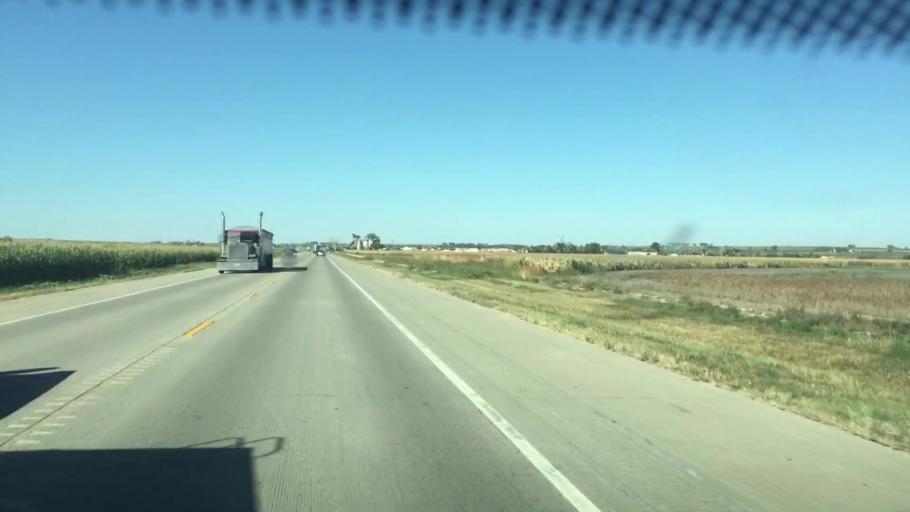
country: US
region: Colorado
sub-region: Prowers County
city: Lamar
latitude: 38.1336
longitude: -102.7236
